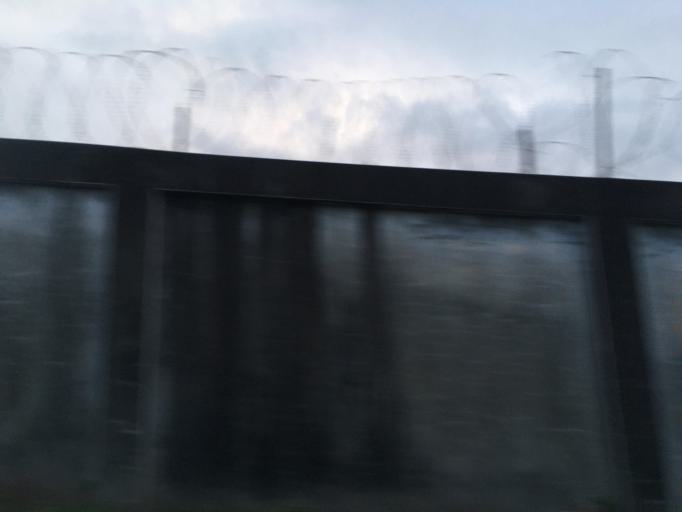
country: TW
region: Taiwan
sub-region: Yilan
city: Yilan
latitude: 24.7564
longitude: 121.7414
